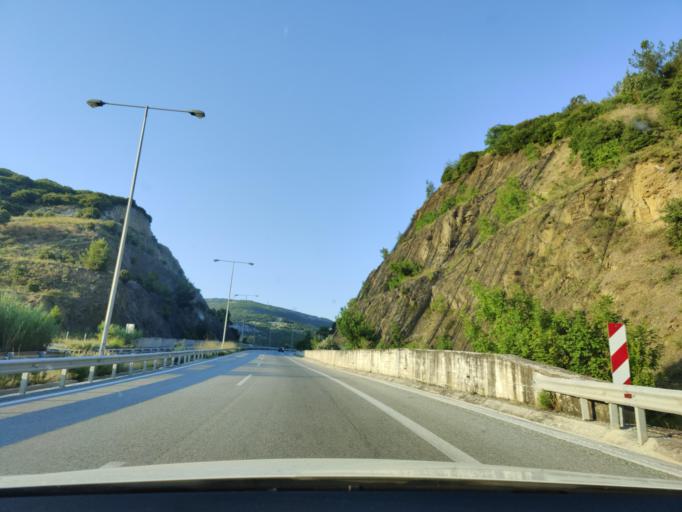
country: GR
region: East Macedonia and Thrace
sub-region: Nomos Kavalas
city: Amygdaleonas
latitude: 40.9523
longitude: 24.3811
